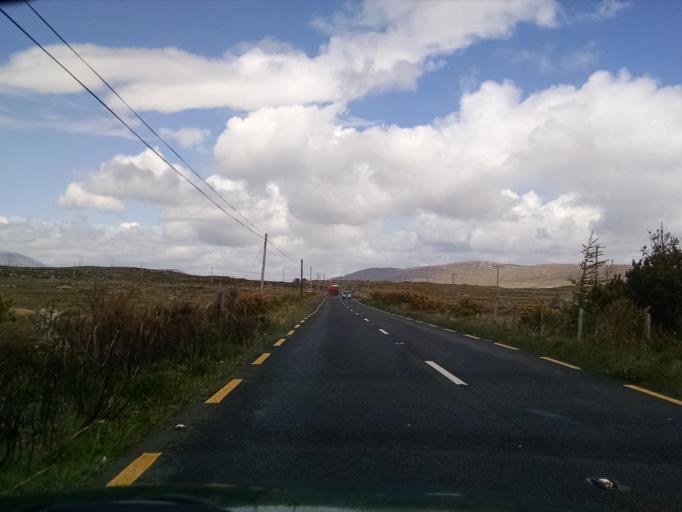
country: IE
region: Connaught
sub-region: County Galway
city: Oughterard
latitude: 53.3461
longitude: -9.5441
